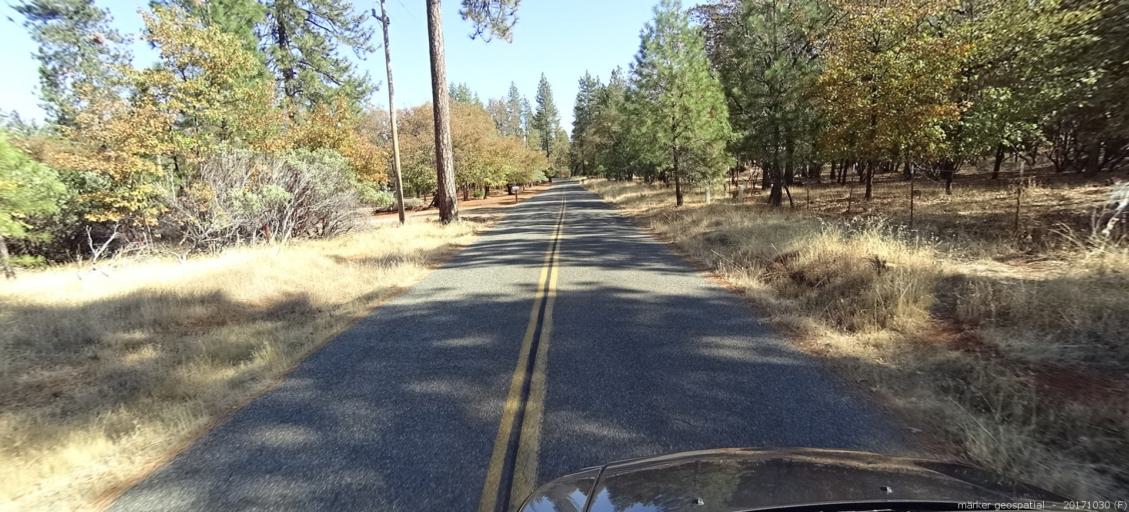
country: US
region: California
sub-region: Shasta County
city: Shingletown
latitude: 40.6010
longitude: -121.9664
